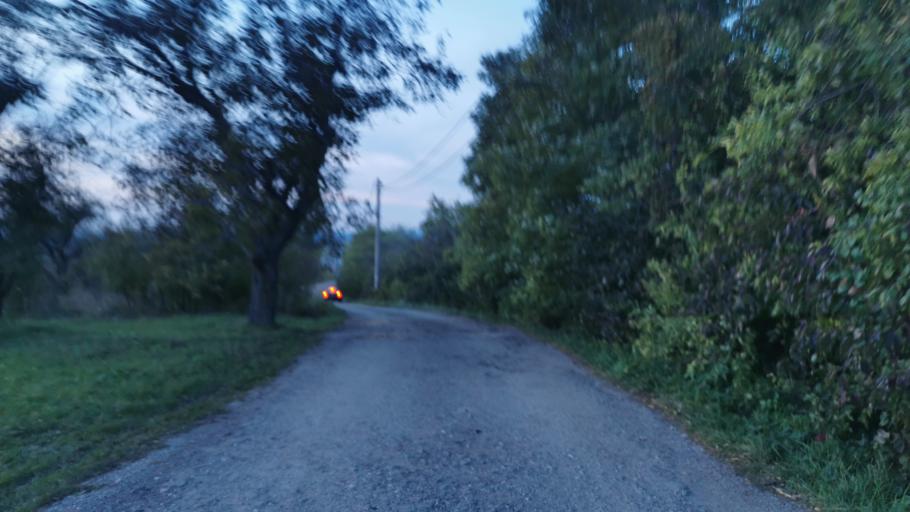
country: SK
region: Trnavsky
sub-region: Okres Skalica
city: Skalica
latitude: 48.8270
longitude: 17.2335
